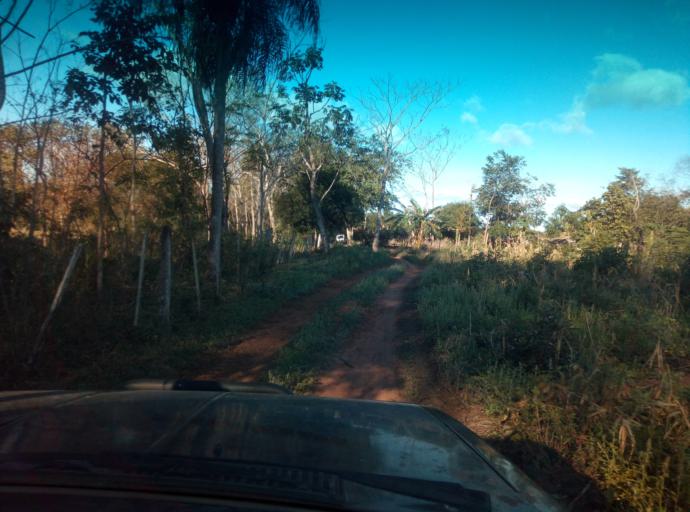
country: PY
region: Caaguazu
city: Carayao
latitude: -25.1822
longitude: -56.2647
